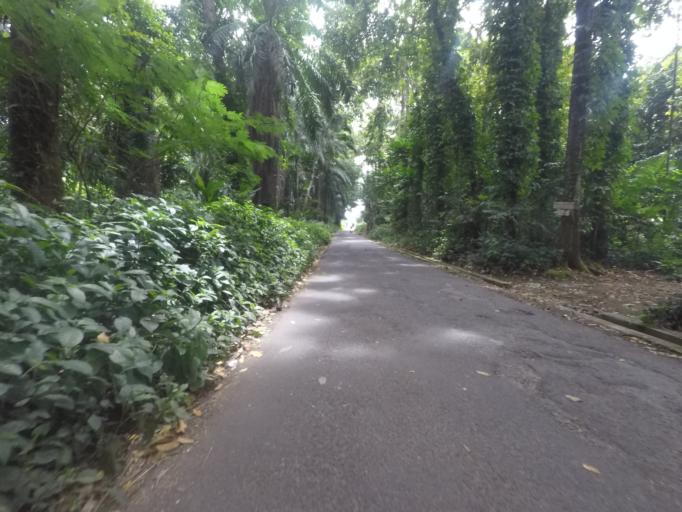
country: ID
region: West Java
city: Ciampea
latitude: -6.5569
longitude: 106.7518
